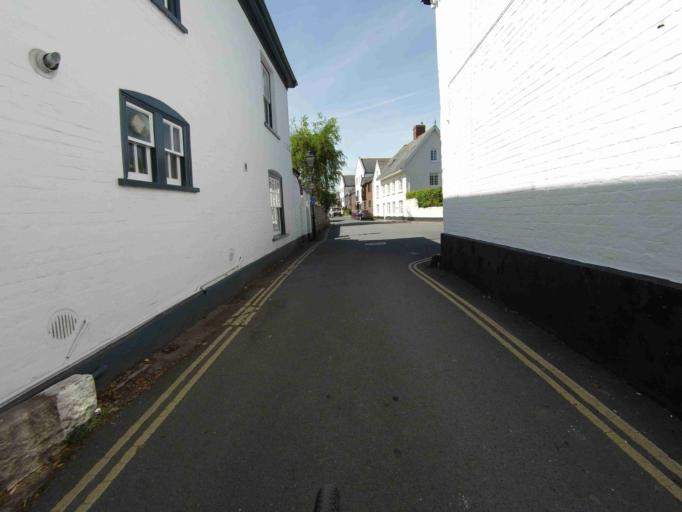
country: GB
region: England
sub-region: Devon
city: Topsham
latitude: 50.6842
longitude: -3.4681
